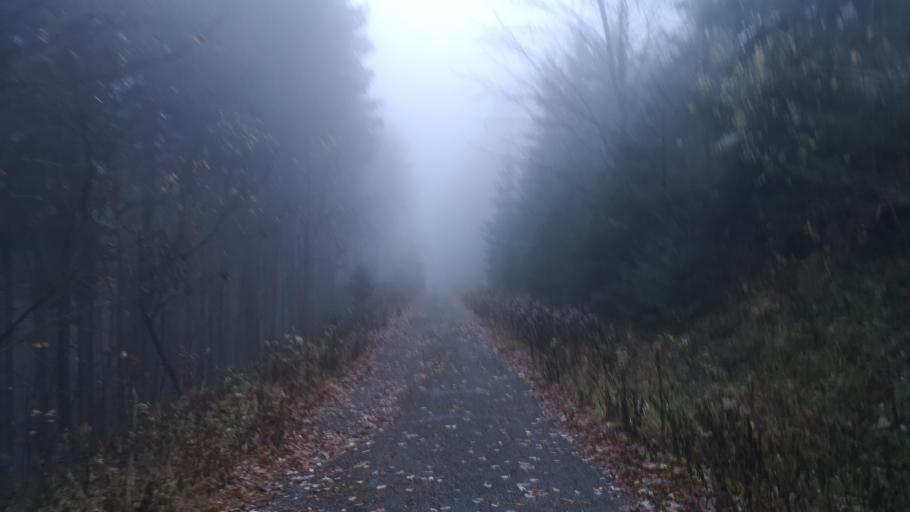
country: SK
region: Banskobystricky
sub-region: Okres Ziar nad Hronom
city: Kremnica
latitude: 48.7601
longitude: 18.9340
